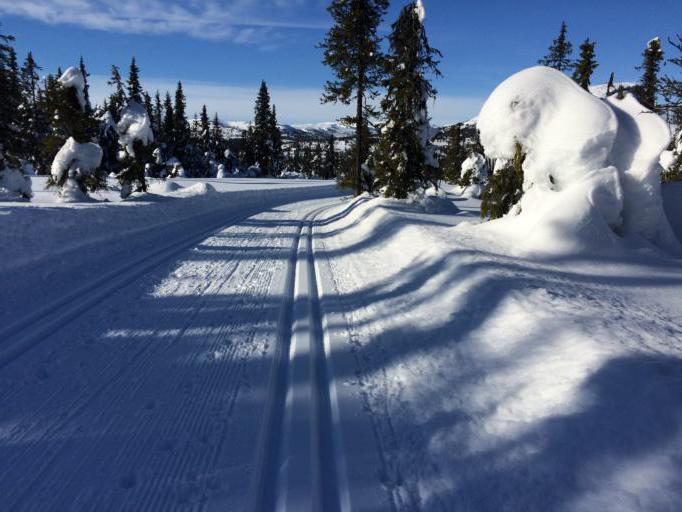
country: NO
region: Oppland
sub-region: Gausdal
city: Segalstad bru
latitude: 61.3206
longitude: 10.0882
